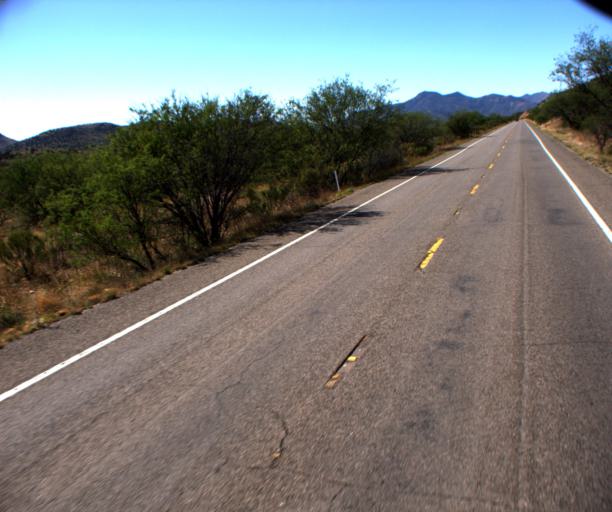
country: US
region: Arizona
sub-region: Santa Cruz County
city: Rio Rico
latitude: 31.6115
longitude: -110.7206
